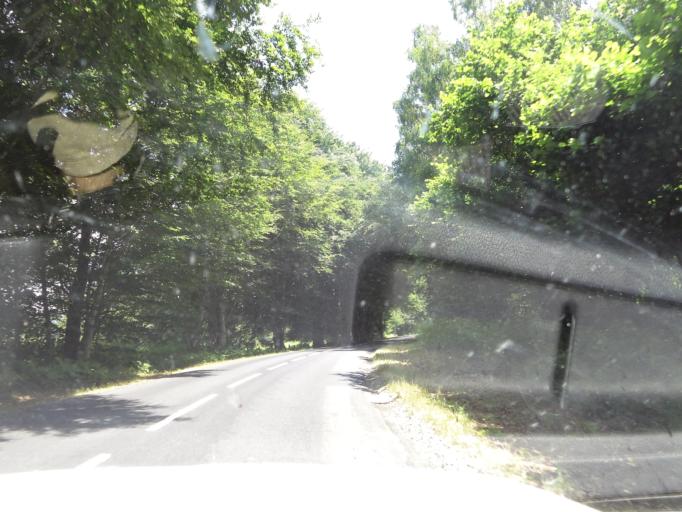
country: FR
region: Auvergne
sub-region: Departement du Puy-de-Dome
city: Orcines
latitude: 45.7646
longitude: 2.9273
